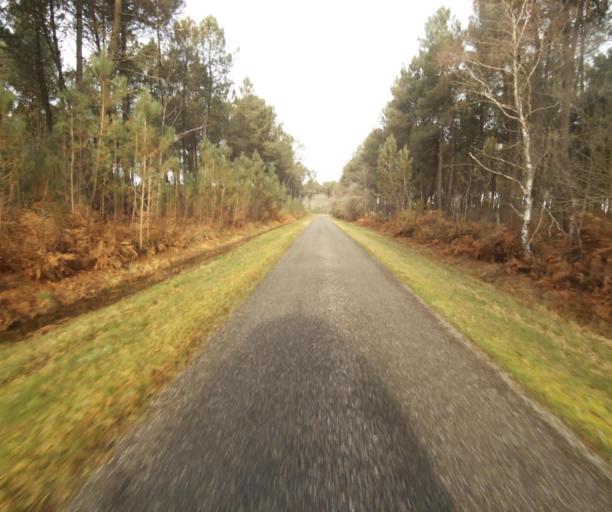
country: FR
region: Aquitaine
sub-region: Departement des Landes
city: Gabarret
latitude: 44.0684
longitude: 0.0912
